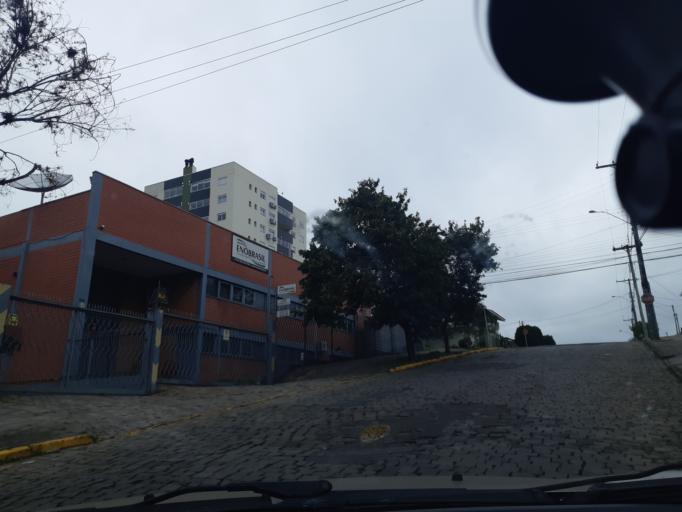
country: BR
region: Rio Grande do Sul
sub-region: Caxias Do Sul
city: Caxias do Sul
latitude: -29.1547
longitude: -51.2067
